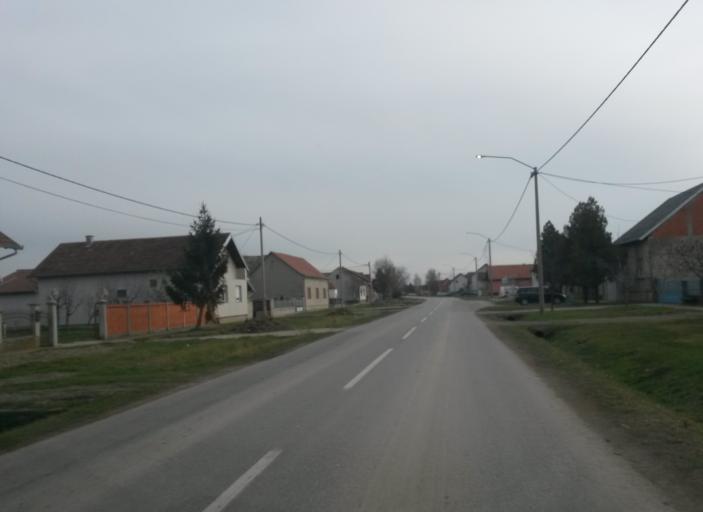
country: HR
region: Osjecko-Baranjska
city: Antunovac
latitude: 45.4836
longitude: 18.6404
